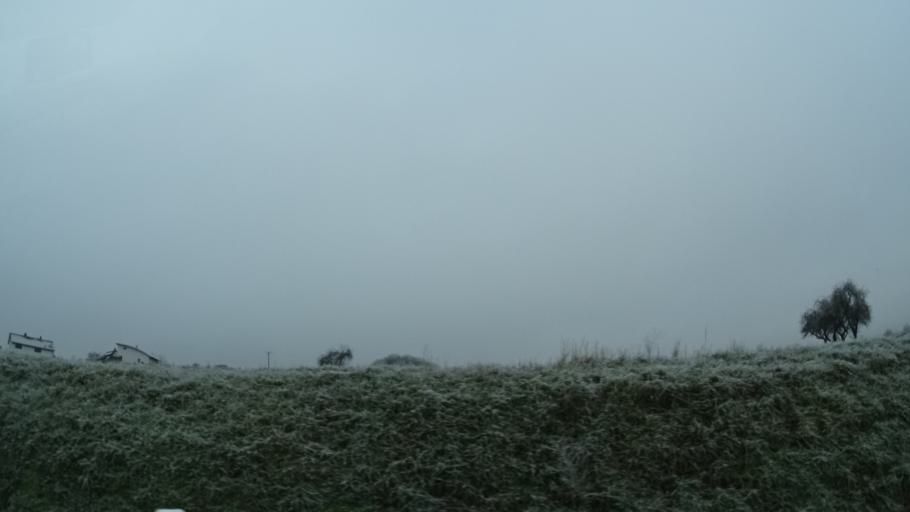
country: DE
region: Bavaria
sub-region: Regierungsbezirk Unterfranken
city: Burgpreppach
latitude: 50.1442
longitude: 10.6540
